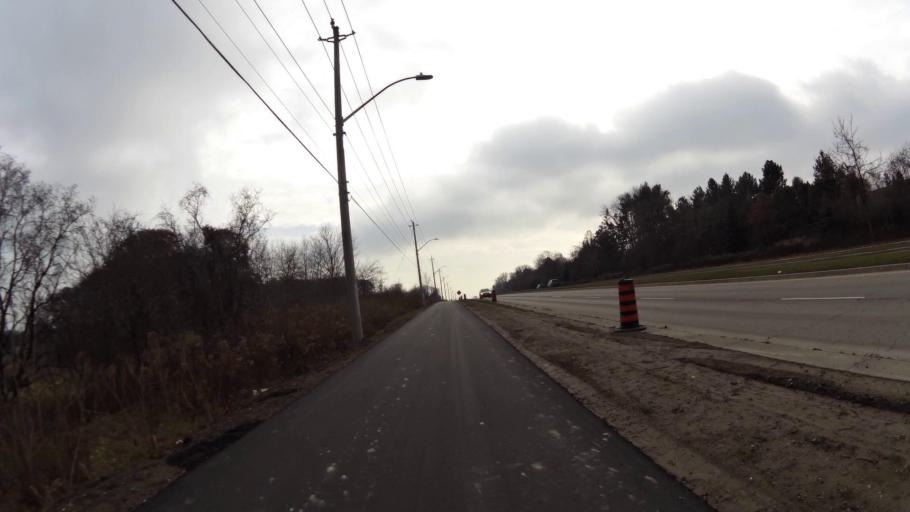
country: CA
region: Ontario
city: Kitchener
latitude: 43.4134
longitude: -80.4648
